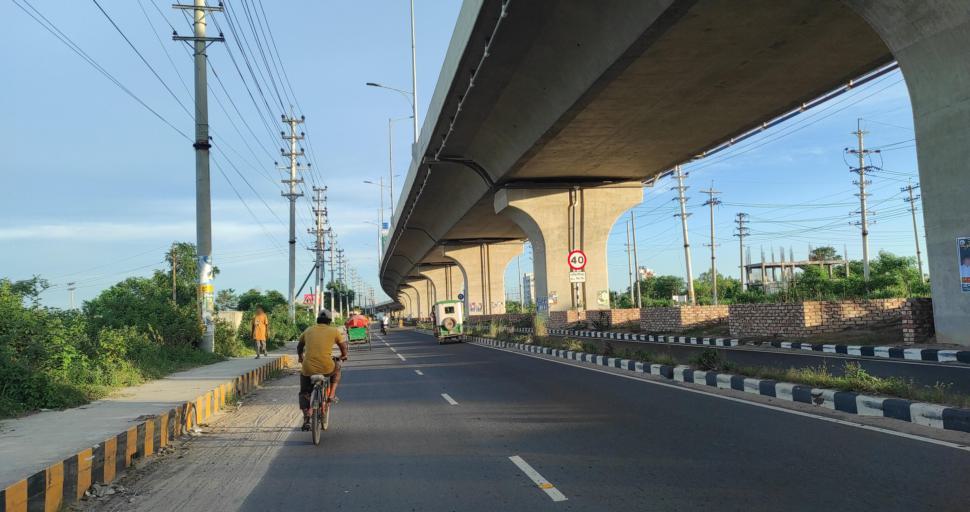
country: BD
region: Dhaka
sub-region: Dhaka
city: Dhaka
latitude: 23.6814
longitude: 90.4033
